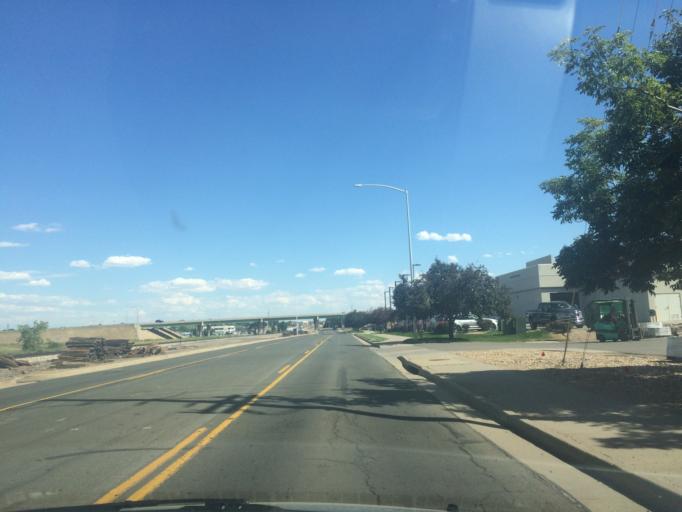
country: US
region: Colorado
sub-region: Broomfield County
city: Broomfield
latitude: 39.9201
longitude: -105.0949
